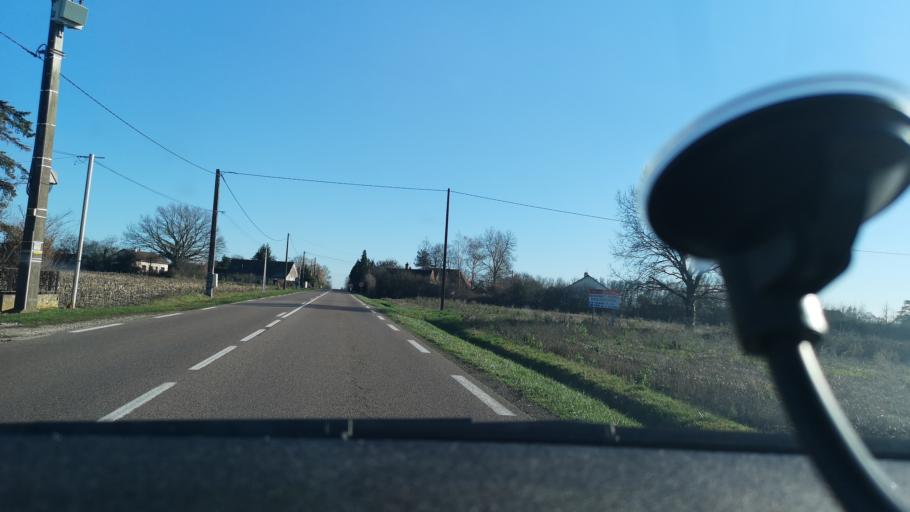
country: FR
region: Bourgogne
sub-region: Departement de Saone-et-Loire
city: Ouroux-sur-Saone
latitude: 46.7581
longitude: 5.0006
